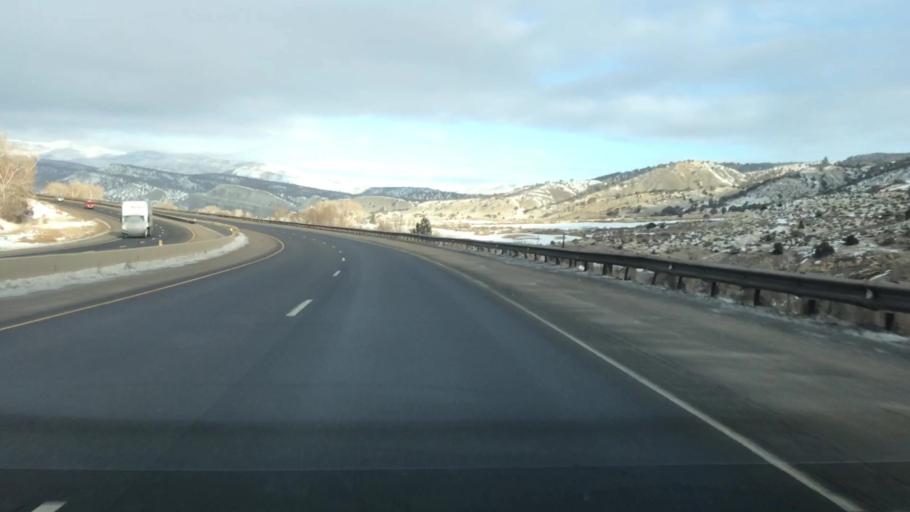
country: US
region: Colorado
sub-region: Eagle County
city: Edwards
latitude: 39.6802
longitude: -106.6484
